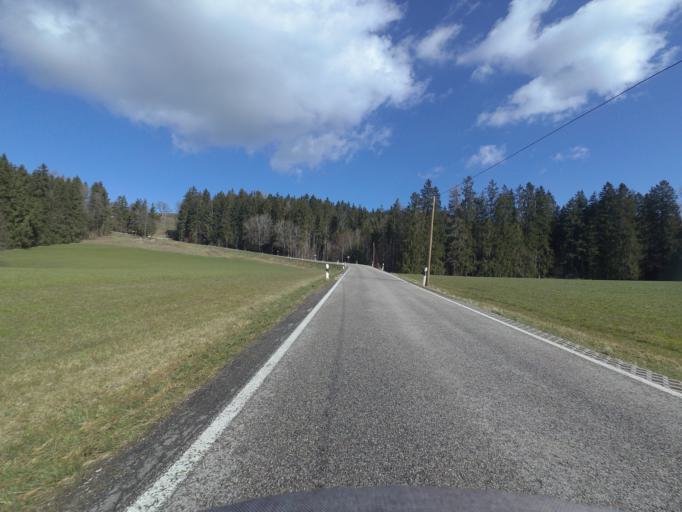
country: DE
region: Bavaria
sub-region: Upper Bavaria
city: Piding
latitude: 47.7853
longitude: 12.9040
